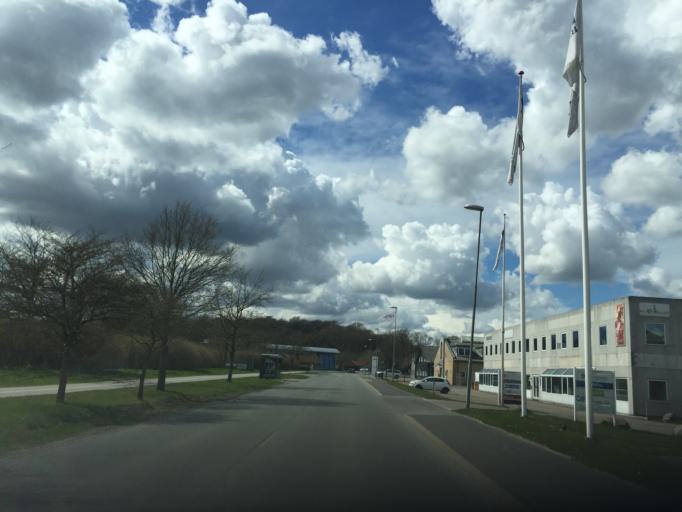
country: DK
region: South Denmark
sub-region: Odense Kommune
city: Odense
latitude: 55.3690
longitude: 10.3975
